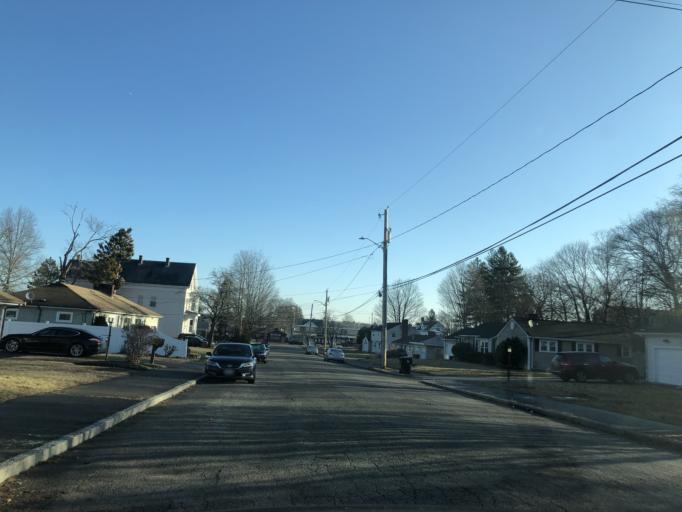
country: US
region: Massachusetts
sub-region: Plymouth County
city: Brockton
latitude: 42.1035
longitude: -71.0263
